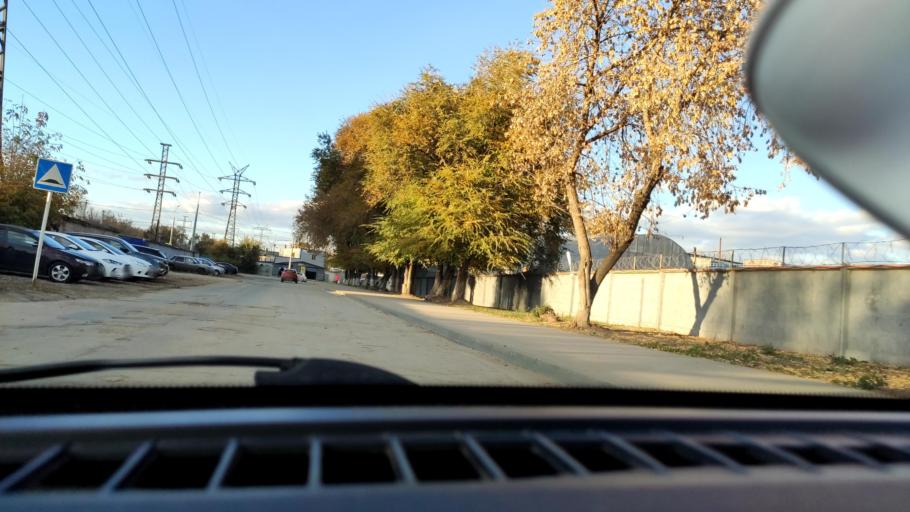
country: RU
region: Samara
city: Smyshlyayevka
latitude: 53.2099
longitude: 50.2863
